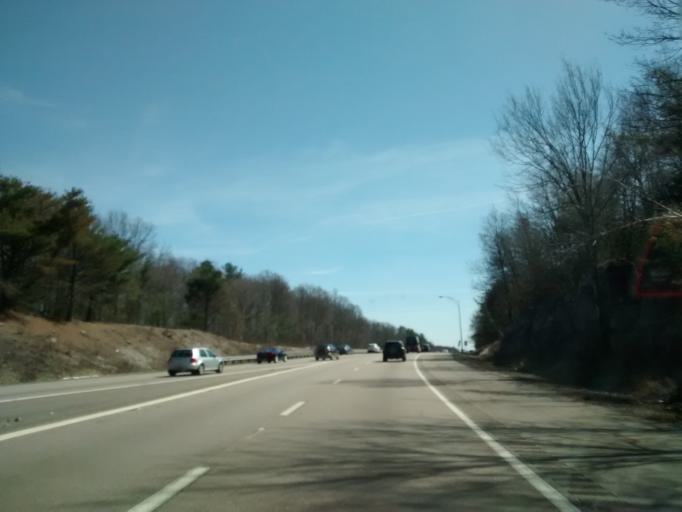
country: US
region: Massachusetts
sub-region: Norfolk County
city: Milton
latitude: 42.1992
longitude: -71.0791
